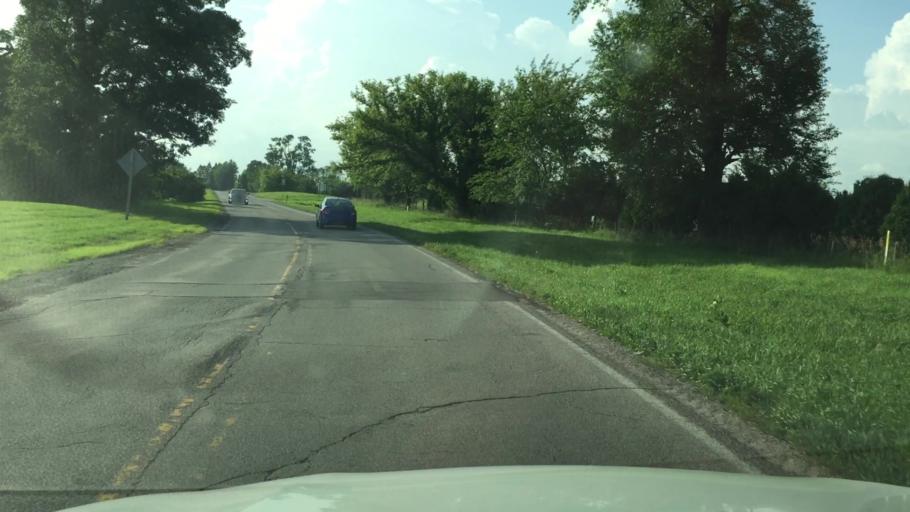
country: US
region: Iowa
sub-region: Linn County
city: Ely
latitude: 41.8365
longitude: -91.6368
